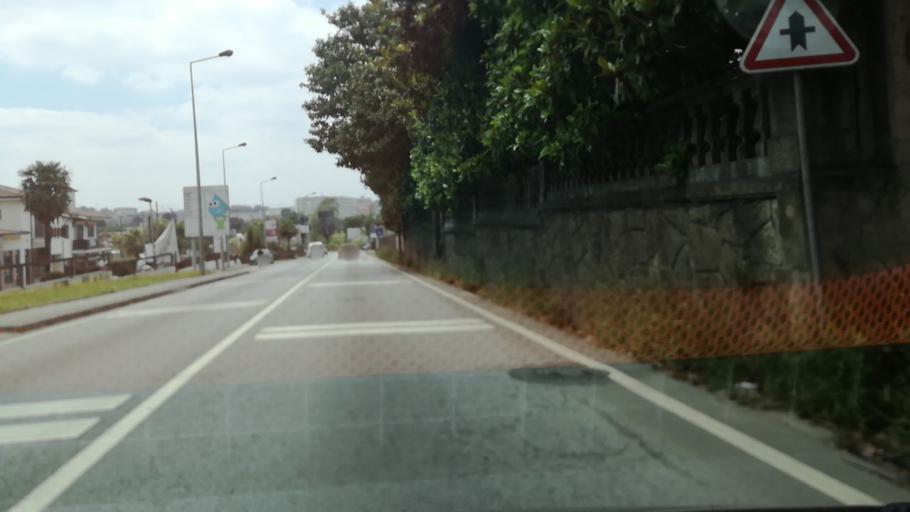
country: PT
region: Braga
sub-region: Vila Nova de Famalicao
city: Ferreiros
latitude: 41.3484
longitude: -8.5557
